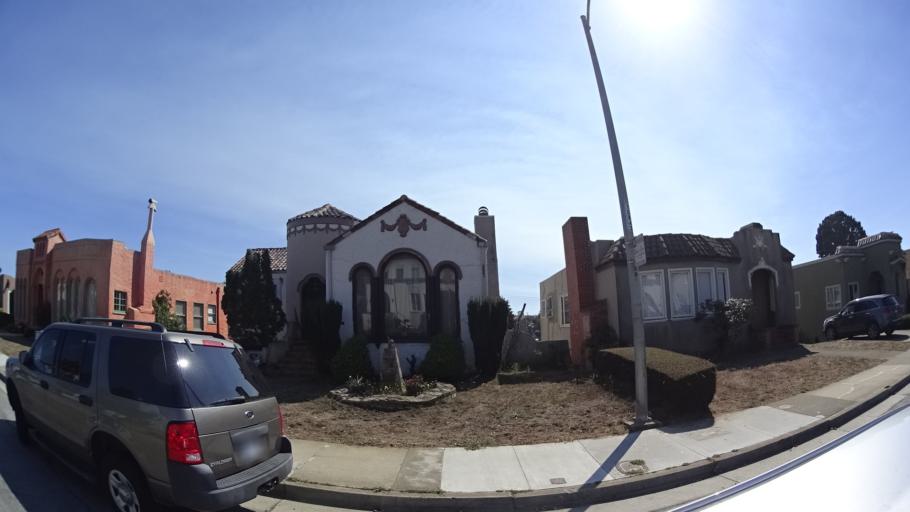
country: US
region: California
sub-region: San Mateo County
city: Daly City
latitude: 37.7257
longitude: -122.4683
